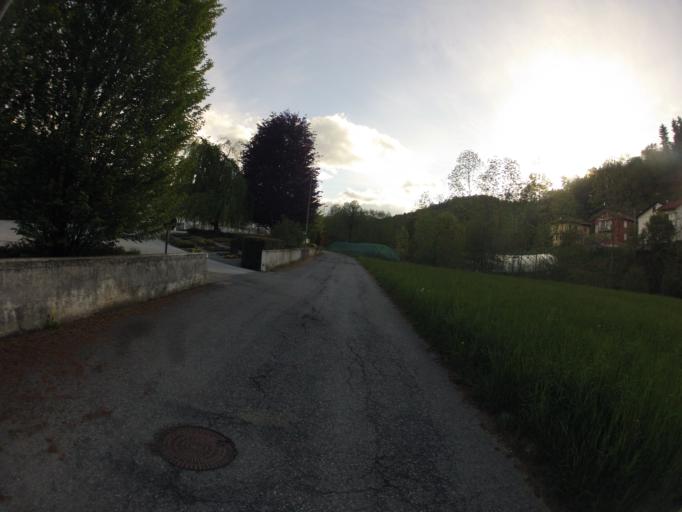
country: IT
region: Piedmont
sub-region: Provincia di Cuneo
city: Peveragno
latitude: 44.3201
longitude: 7.5976
